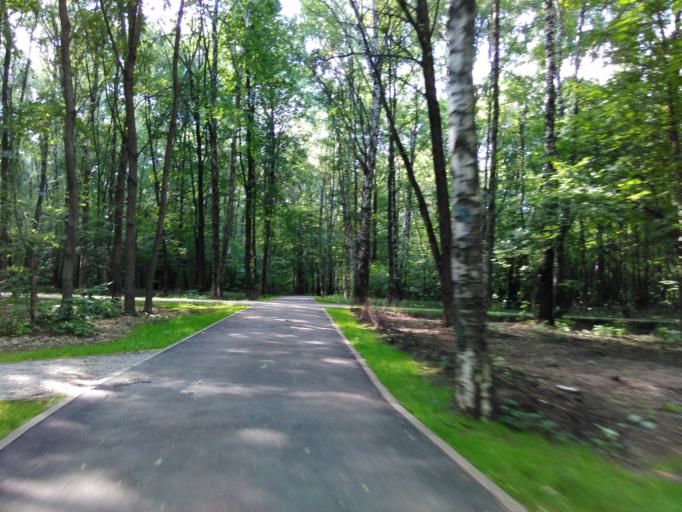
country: RU
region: Moscow
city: Troparevo
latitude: 55.6550
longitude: 37.5113
